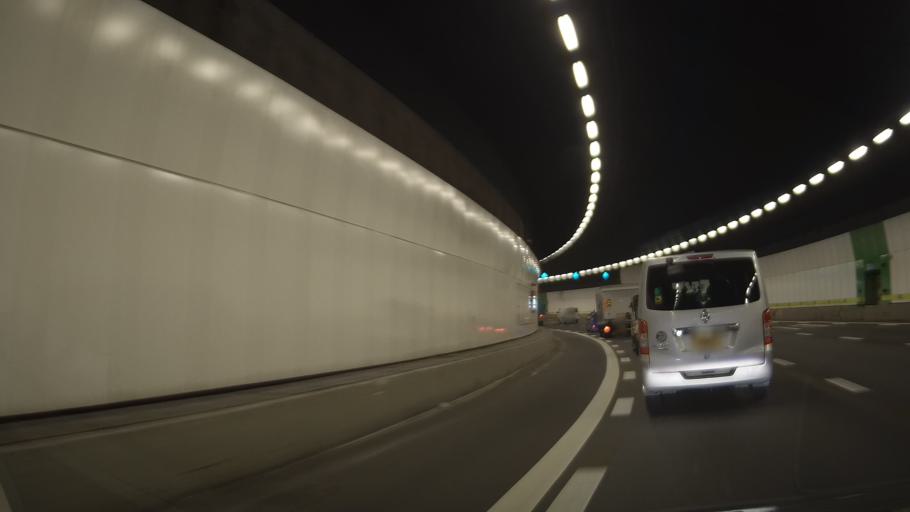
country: SG
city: Singapore
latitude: 1.3360
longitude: 103.8895
